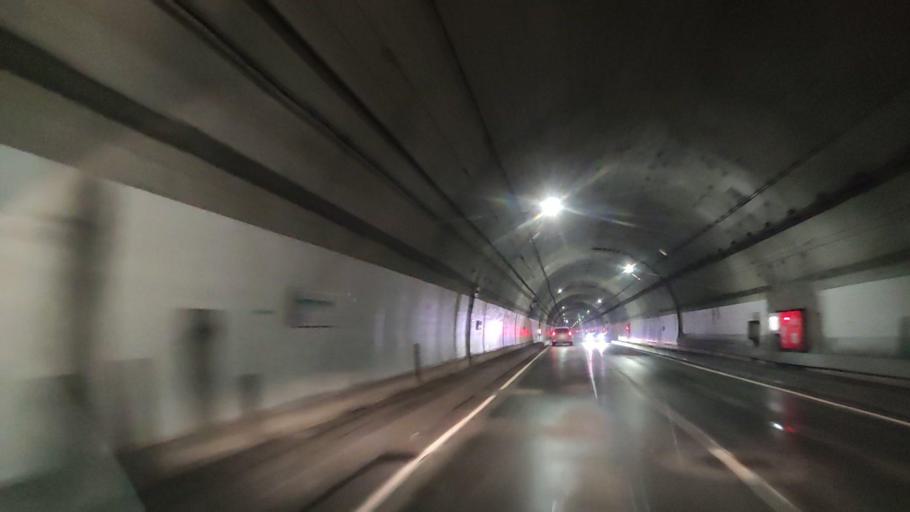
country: JP
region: Hokkaido
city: Rumoi
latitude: 43.7072
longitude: 141.3341
